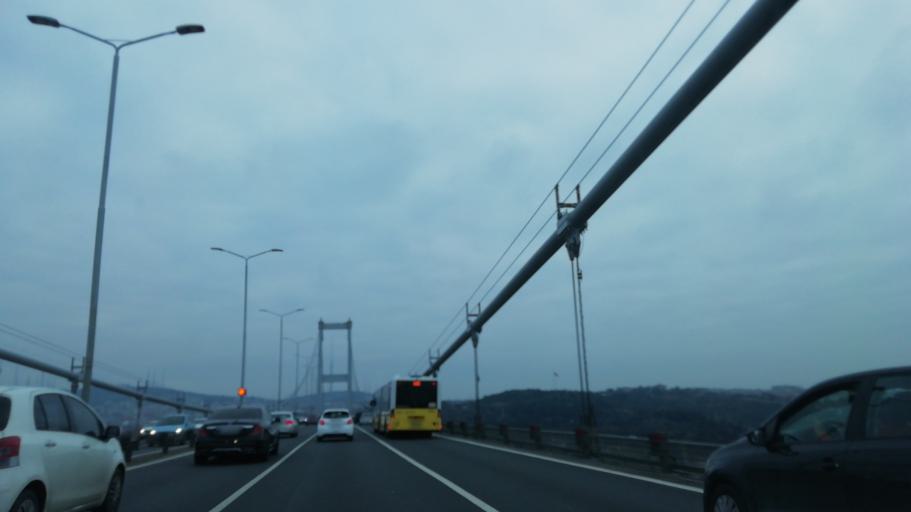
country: TR
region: Istanbul
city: UEskuedar
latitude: 41.0465
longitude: 29.0333
